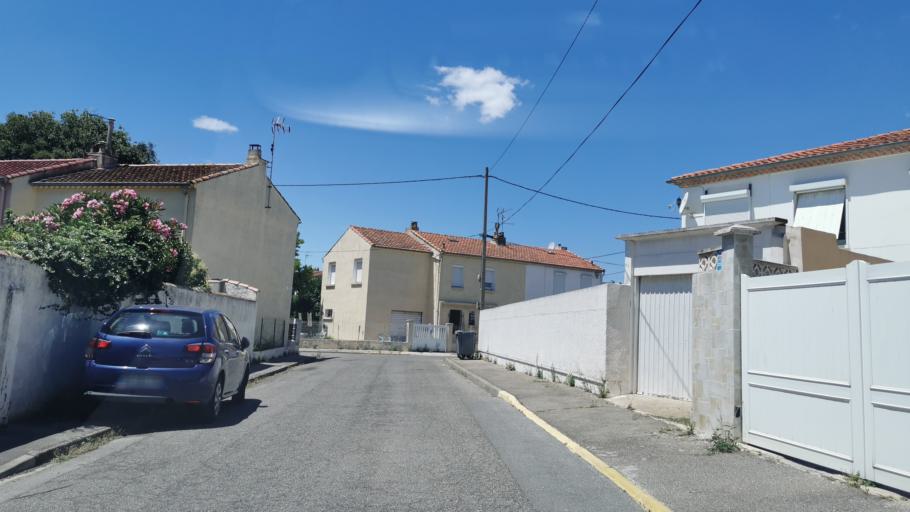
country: FR
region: Languedoc-Roussillon
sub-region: Departement de l'Aude
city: Narbonne
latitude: 43.1878
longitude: 3.0202
